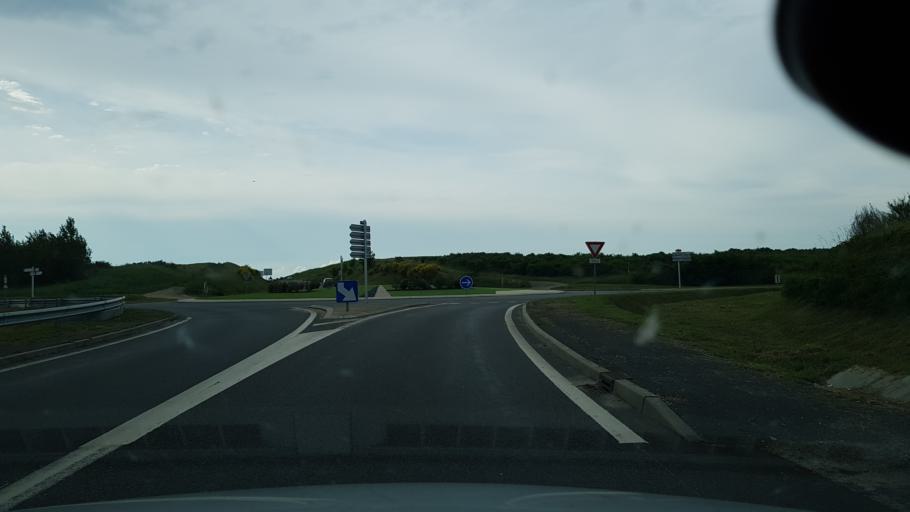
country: FR
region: Centre
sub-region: Departement du Loir-et-Cher
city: Contres
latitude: 47.4215
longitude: 1.4496
